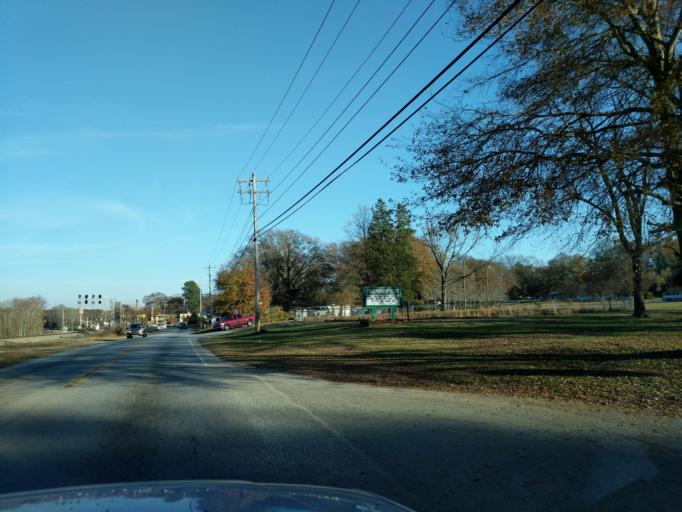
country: US
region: South Carolina
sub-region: Spartanburg County
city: Fairforest
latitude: 34.9563
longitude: -82.0021
